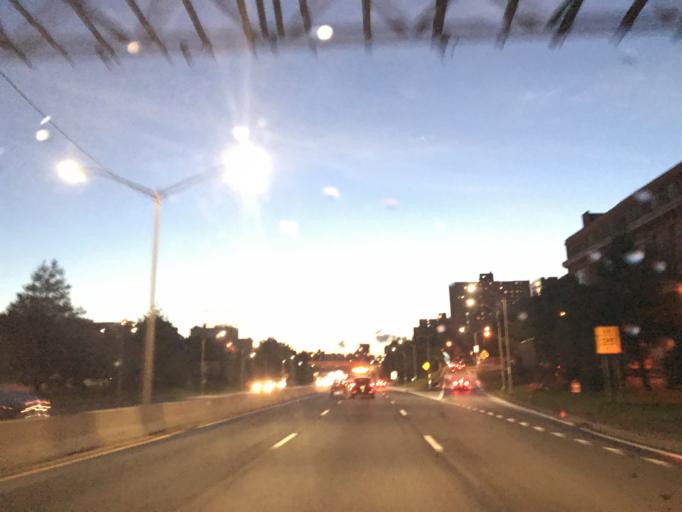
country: US
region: New York
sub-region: New York County
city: Manhattan
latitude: 40.8055
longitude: -73.9209
